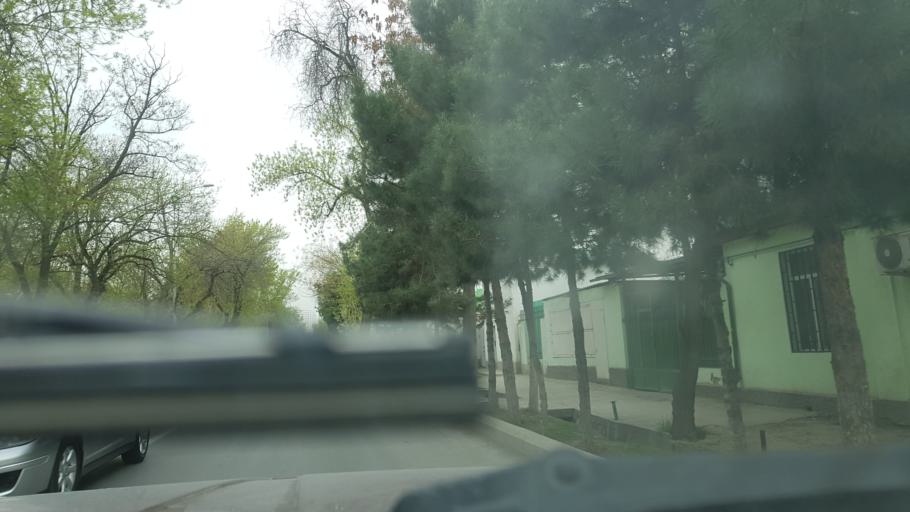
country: TM
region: Ahal
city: Ashgabat
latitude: 37.9515
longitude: 58.3629
